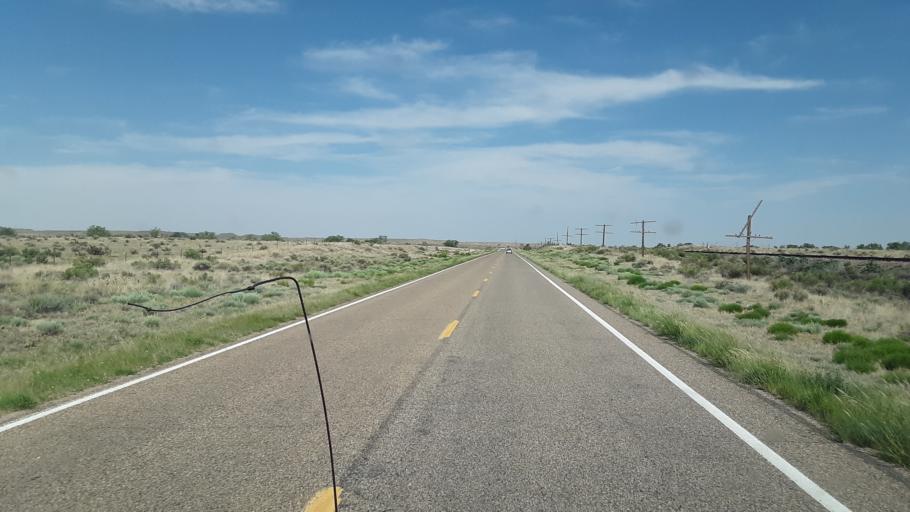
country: US
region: Colorado
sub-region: Otero County
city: Fowler
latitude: 38.1928
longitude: -104.1517
